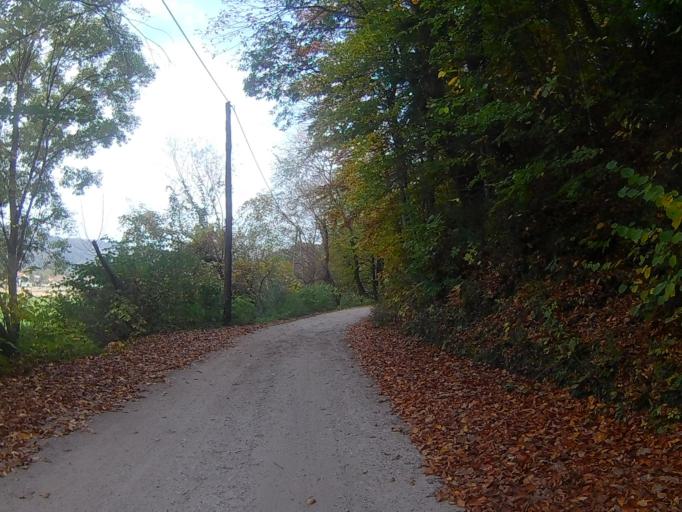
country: SI
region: Ruse
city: Ruse
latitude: 46.5440
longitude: 15.5319
